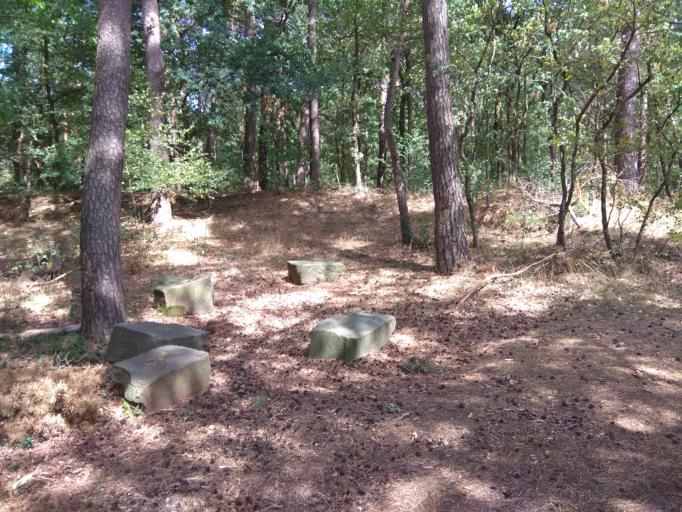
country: DE
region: North Rhine-Westphalia
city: Dorsten
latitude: 51.7237
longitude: 6.9500
